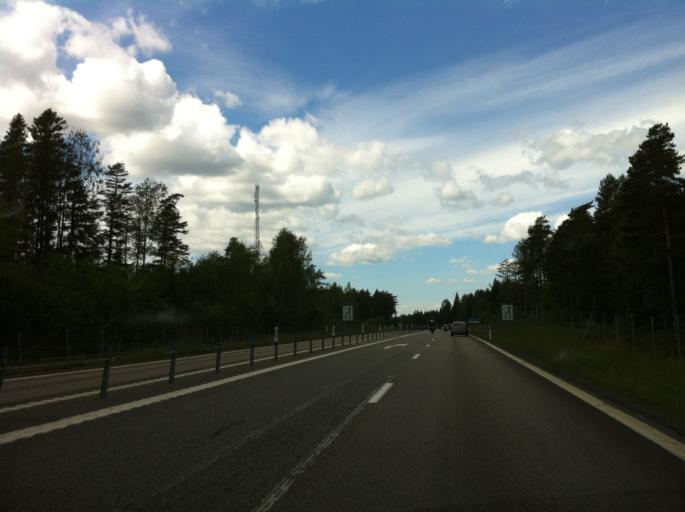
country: SE
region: Vaestra Goetaland
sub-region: Amals Kommun
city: Amal
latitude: 59.0975
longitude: 12.7626
